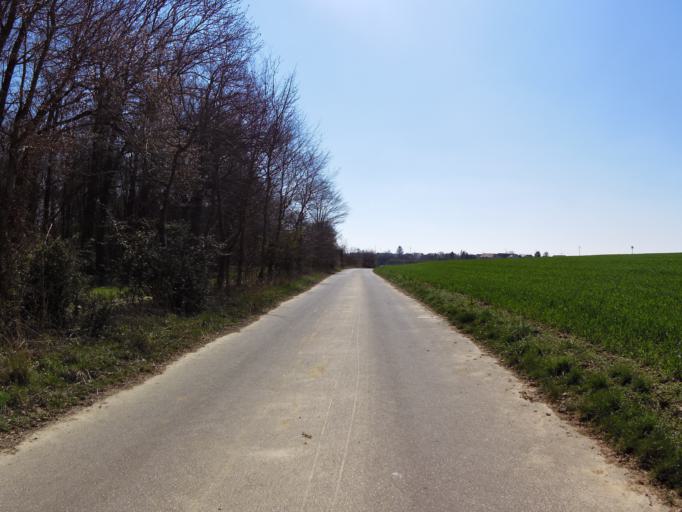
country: DE
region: Bavaria
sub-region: Regierungsbezirk Unterfranken
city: Biebelried
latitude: 49.7718
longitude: 10.0857
